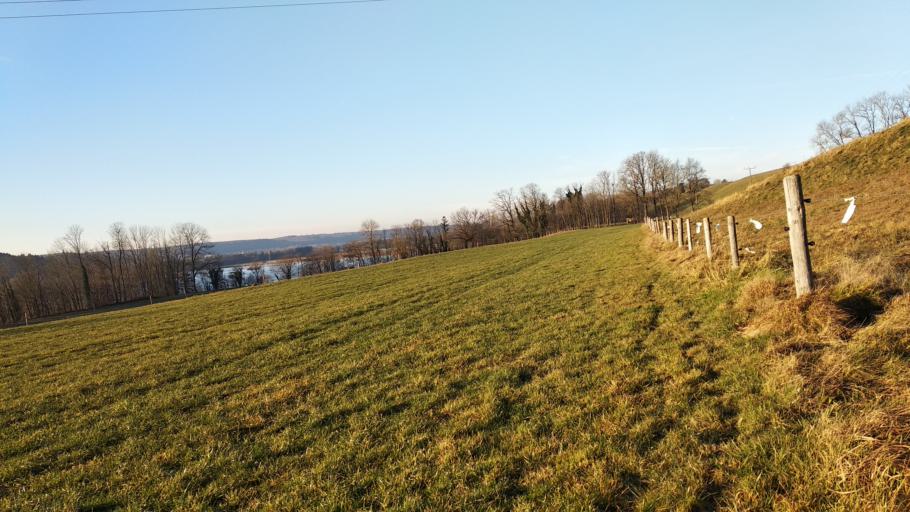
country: DE
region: Bavaria
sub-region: Swabia
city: Lautrach
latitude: 47.9125
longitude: 10.1278
